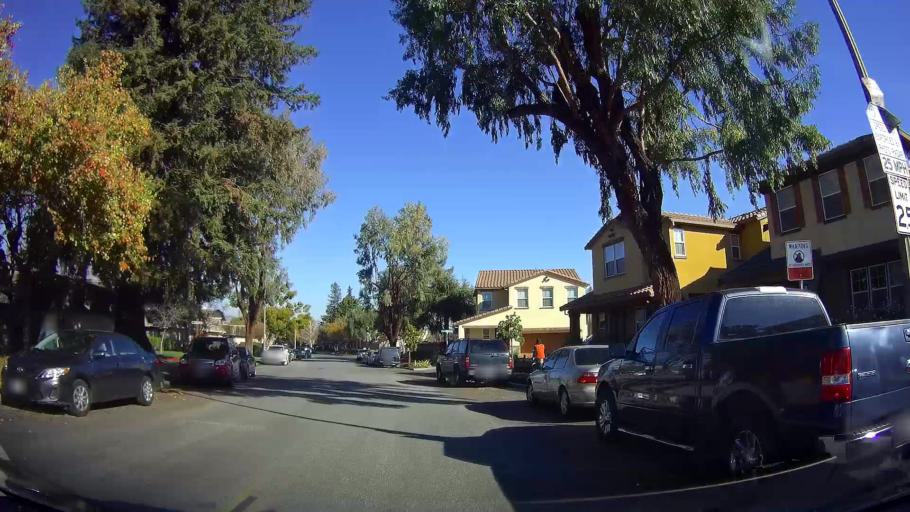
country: US
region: California
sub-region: Santa Clara County
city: Seven Trees
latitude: 37.2630
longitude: -121.8646
